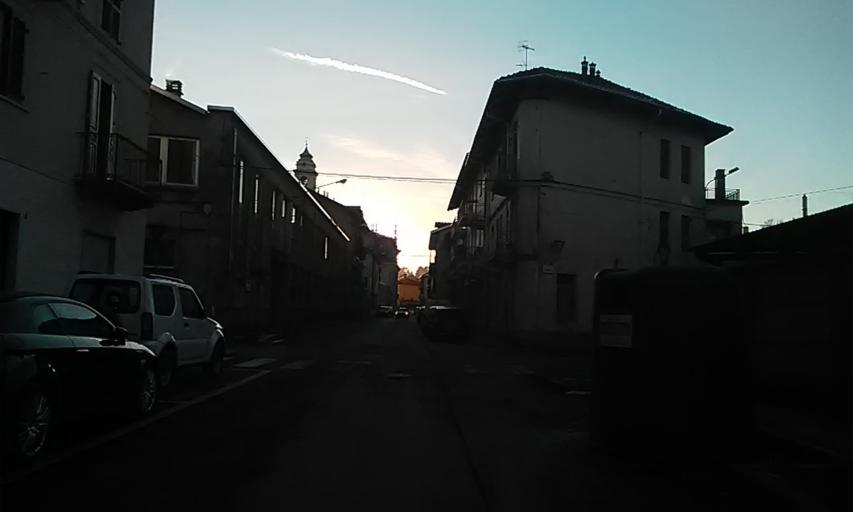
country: IT
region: Piedmont
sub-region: Provincia di Biella
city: Biella
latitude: 45.5739
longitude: 8.0695
